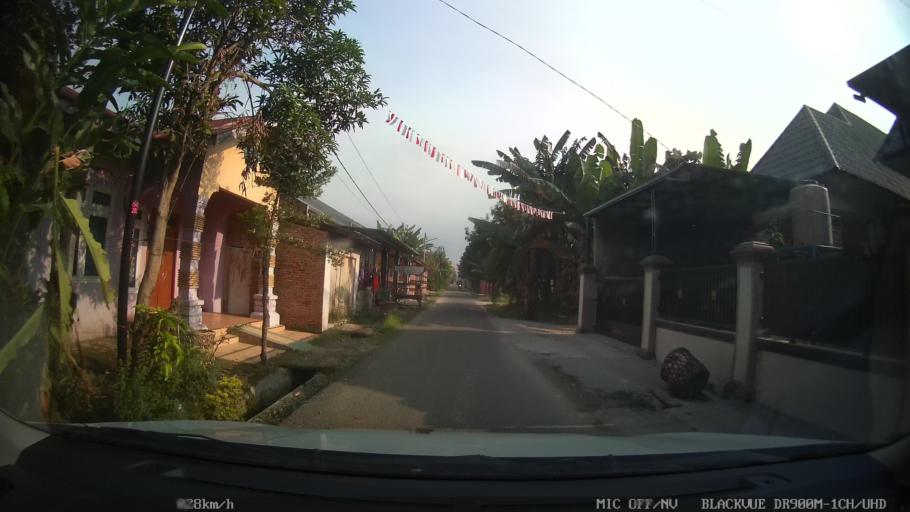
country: ID
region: North Sumatra
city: Binjai
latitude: 3.6205
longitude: 98.5272
